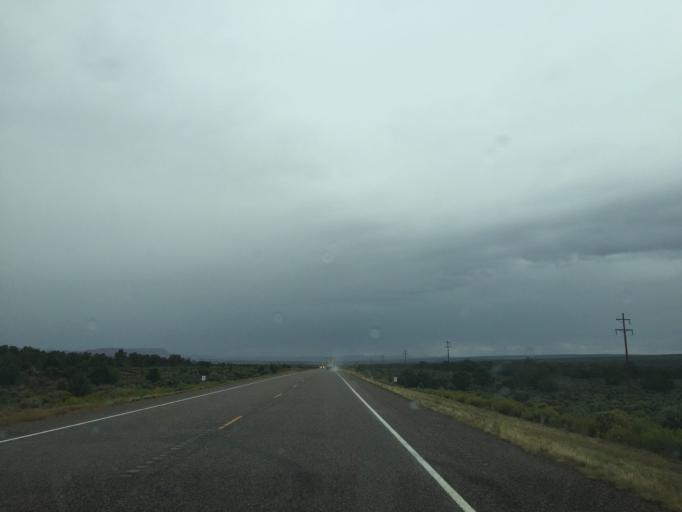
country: US
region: Utah
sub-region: Kane County
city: Kanab
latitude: 37.0791
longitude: -112.1631
